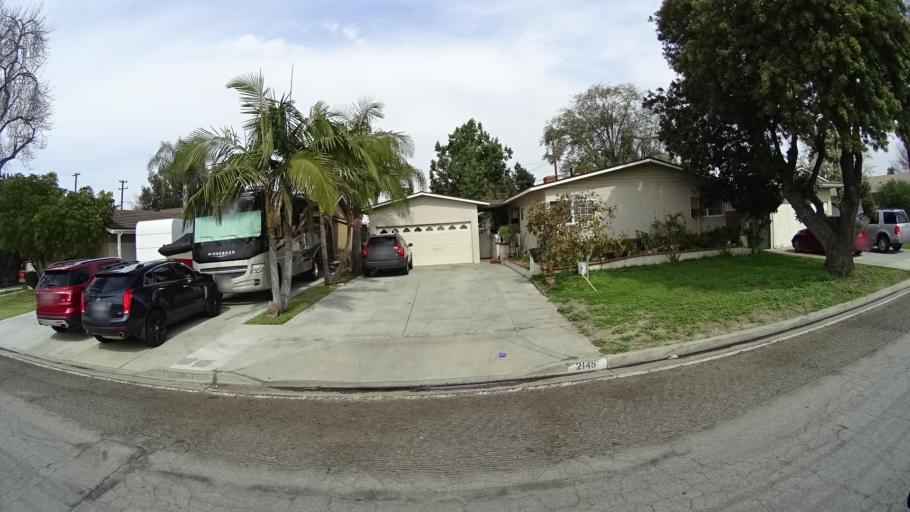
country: US
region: California
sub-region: Orange County
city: Stanton
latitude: 33.8094
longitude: -117.9574
